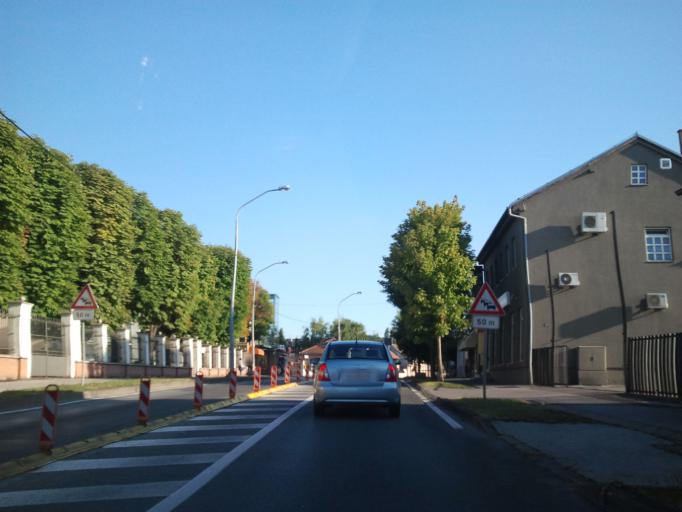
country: HR
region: Sisacko-Moslavacka
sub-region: Grad Sisak
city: Sisak
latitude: 45.4770
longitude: 16.3681
